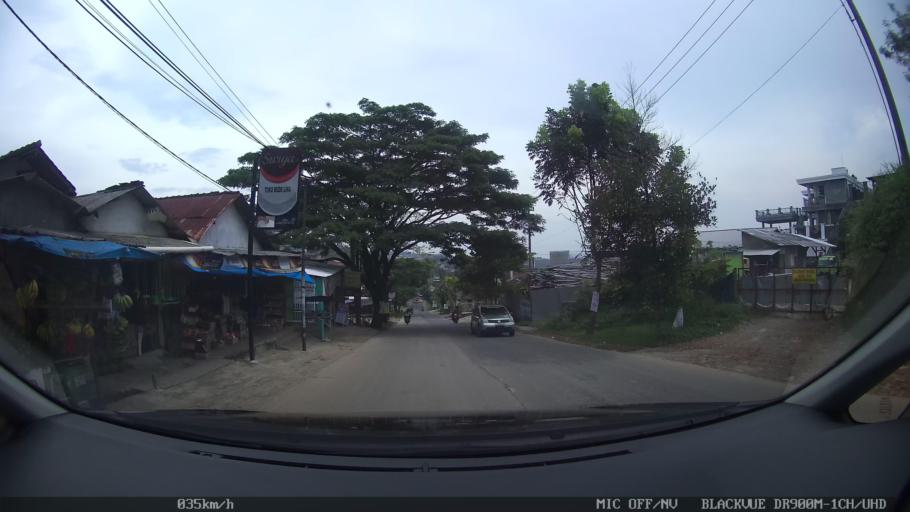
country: ID
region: Lampung
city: Bandarlampung
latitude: -5.4074
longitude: 105.2198
